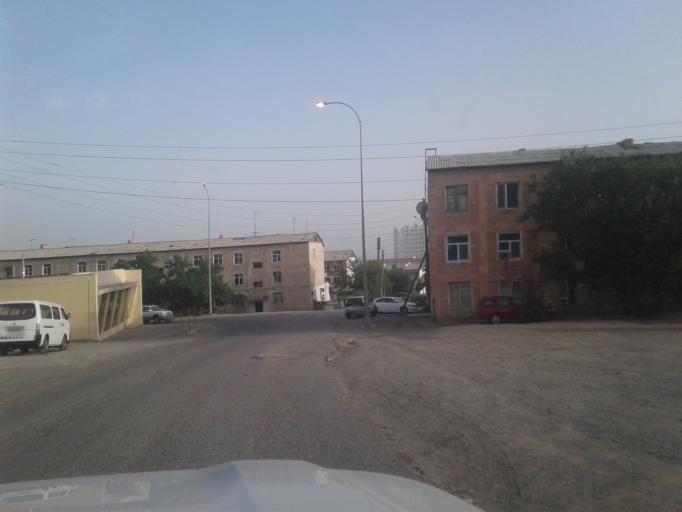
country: TM
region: Balkan
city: Turkmenbasy
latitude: 40.0038
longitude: 52.9647
